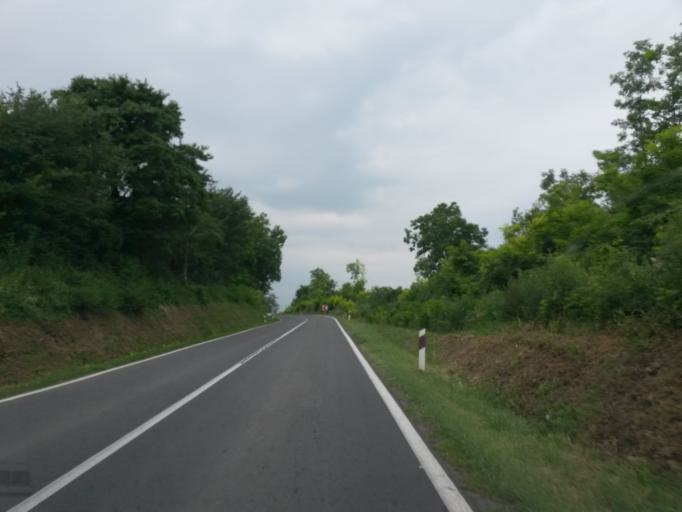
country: HR
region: Vukovarsko-Srijemska
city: Bapska
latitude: 45.2354
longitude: 19.2554
